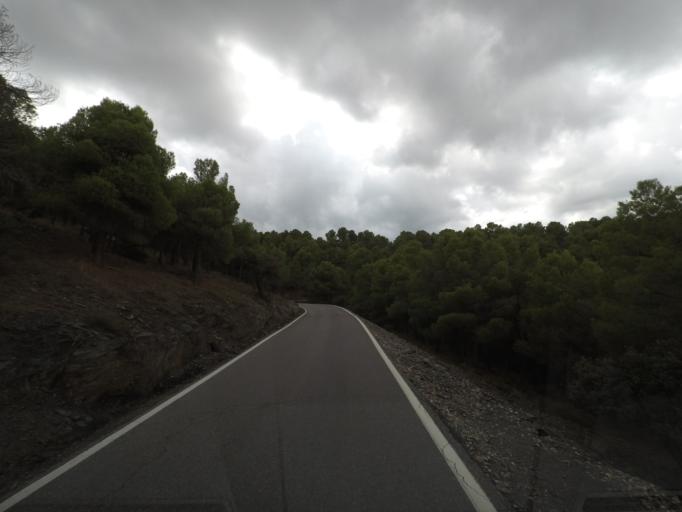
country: ES
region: Andalusia
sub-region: Provincia de Granada
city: Ferreira
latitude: 37.1709
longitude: -3.0496
